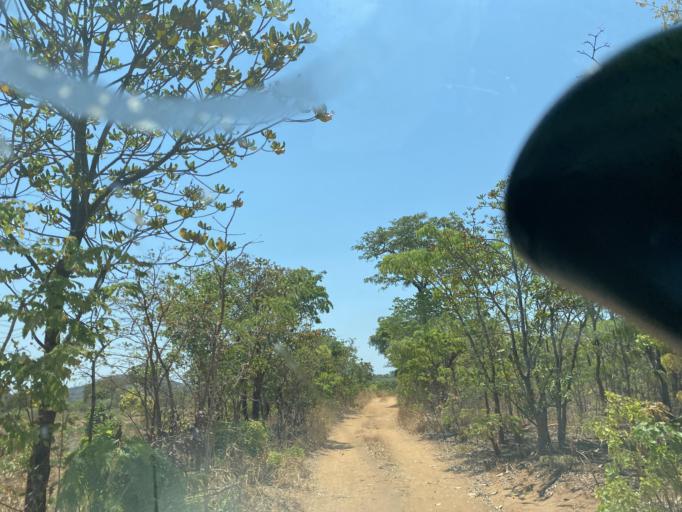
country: ZM
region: Lusaka
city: Chongwe
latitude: -15.4372
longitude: 29.1994
